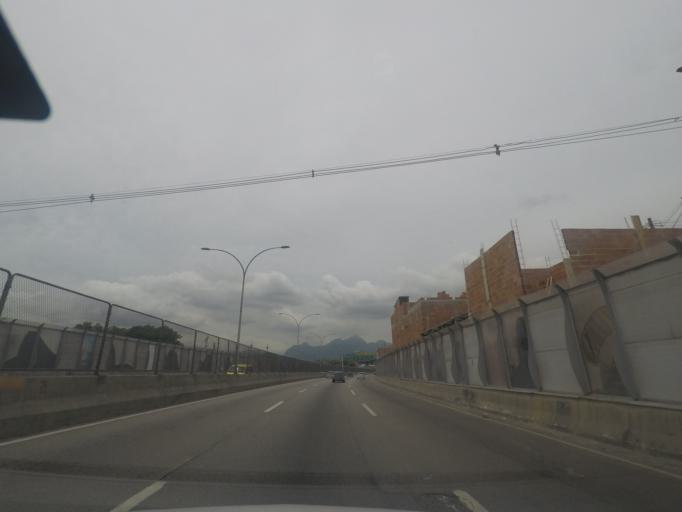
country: BR
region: Rio de Janeiro
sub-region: Rio De Janeiro
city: Rio de Janeiro
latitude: -22.8663
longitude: -43.2401
